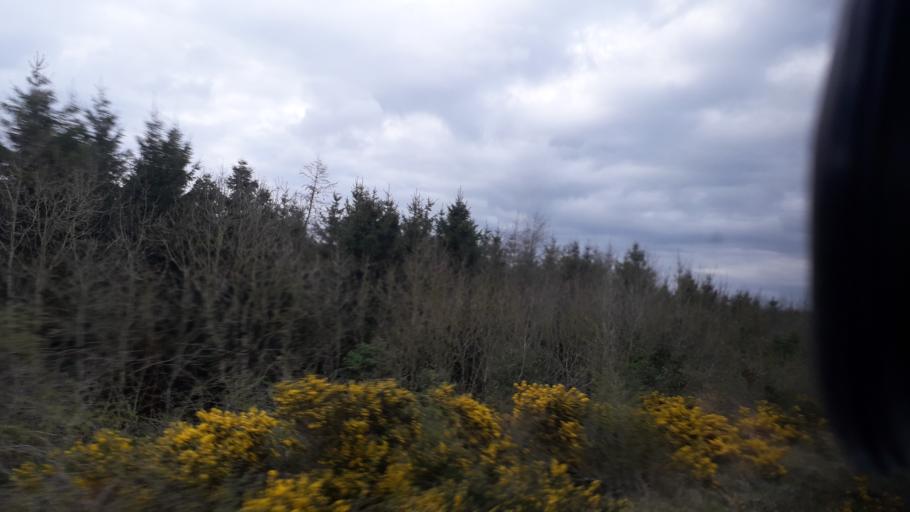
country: IE
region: Leinster
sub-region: An Iarmhi
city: Castlepollard
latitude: 53.6394
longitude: -7.4197
